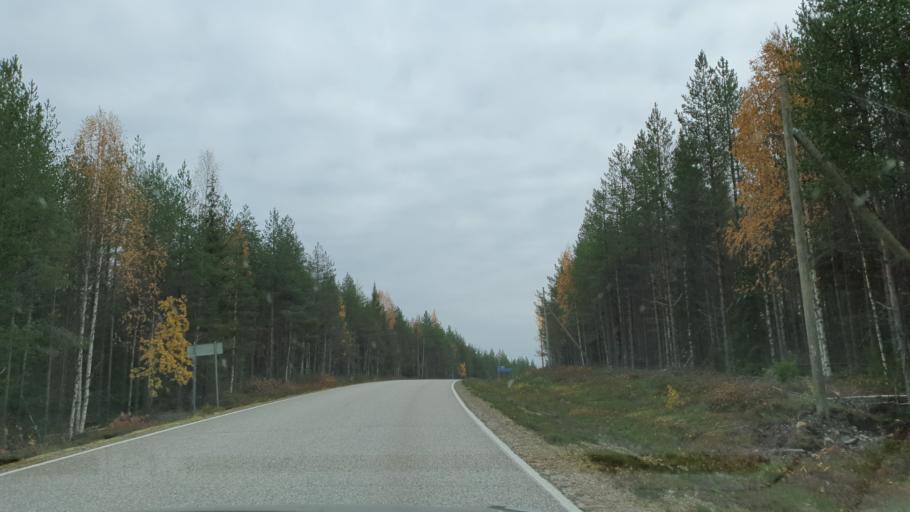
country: FI
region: Kainuu
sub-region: Kajaani
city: Ristijaervi
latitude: 64.4424
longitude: 28.3684
